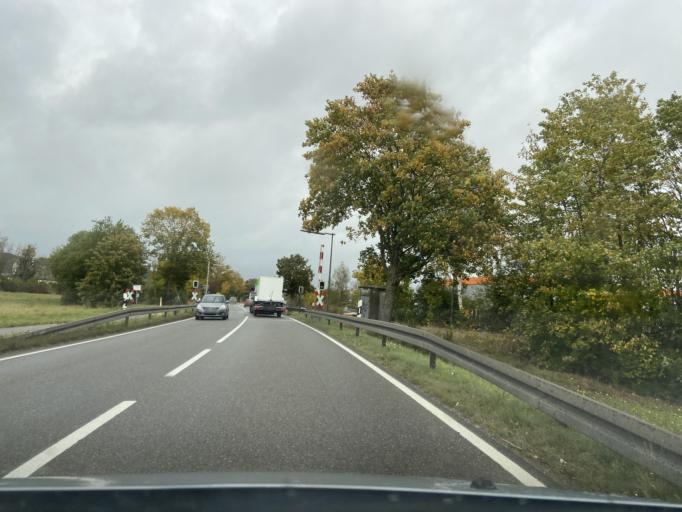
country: DE
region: Baden-Wuerttemberg
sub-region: Tuebingen Region
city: Krauchenwies
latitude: 48.0157
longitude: 9.2350
